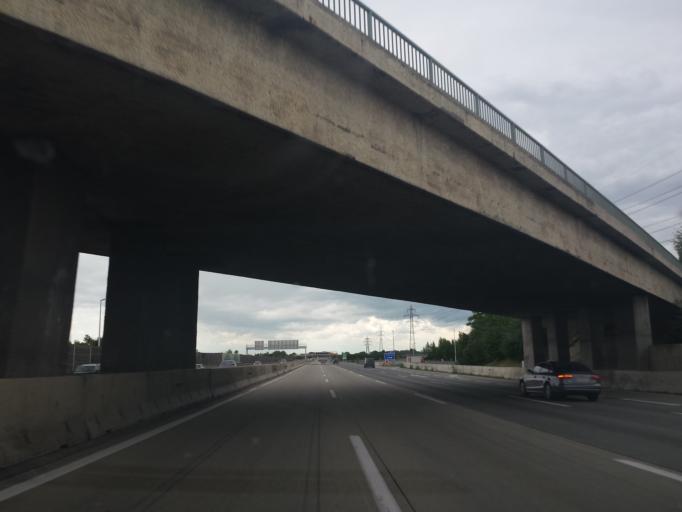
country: AT
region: Lower Austria
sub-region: Politischer Bezirk Modling
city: Laxenburg
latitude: 48.0618
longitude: 16.3397
